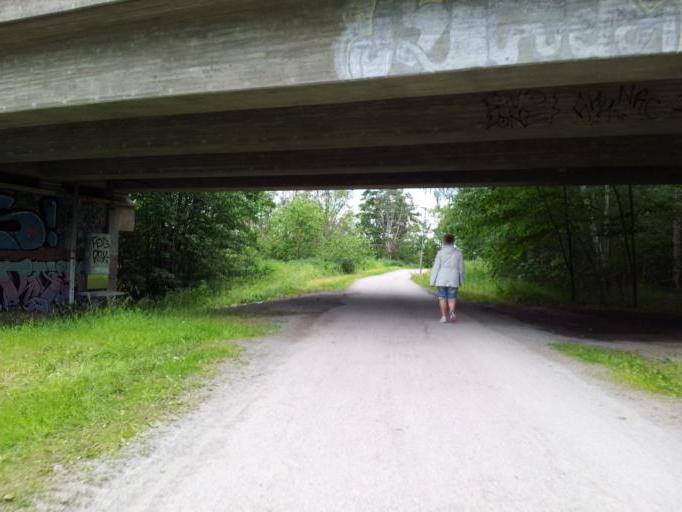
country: SE
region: Uppsala
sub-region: Uppsala Kommun
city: Uppsala
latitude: 59.8419
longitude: 17.6557
